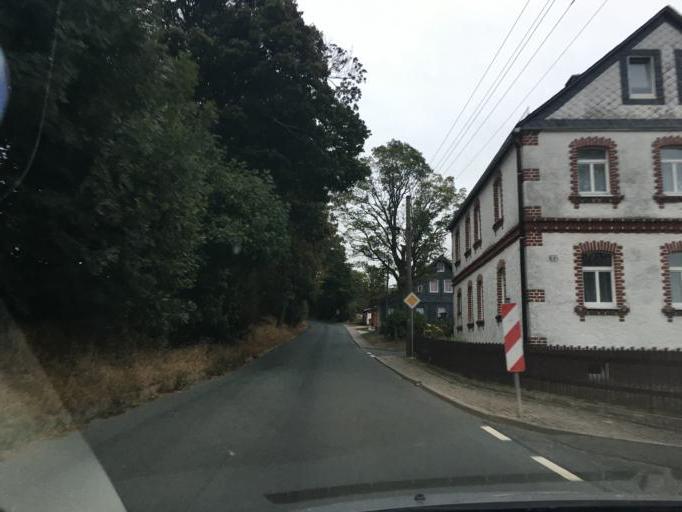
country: DE
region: Thuringia
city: Remptendorf
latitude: 50.4967
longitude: 11.6432
